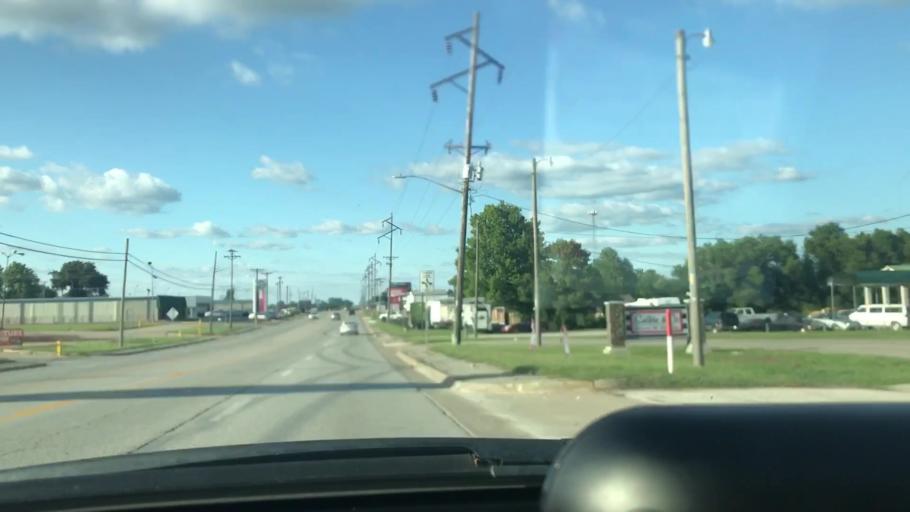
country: US
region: Missouri
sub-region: Pettis County
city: Sedalia
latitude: 38.6779
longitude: -93.2515
